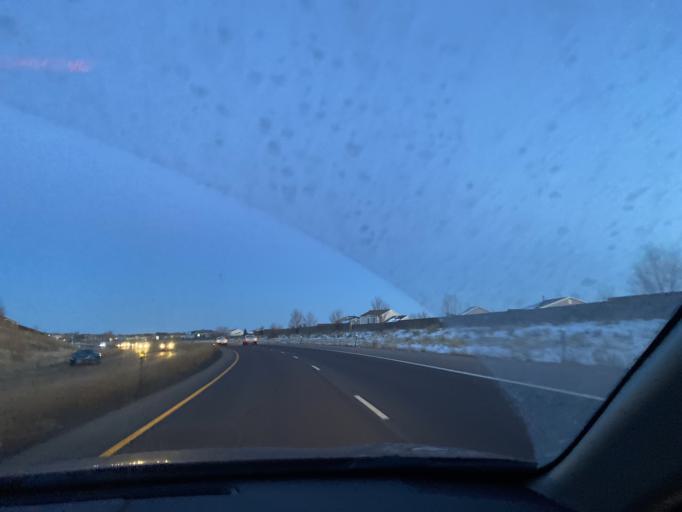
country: US
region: Colorado
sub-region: El Paso County
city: Fountain
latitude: 38.7163
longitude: -104.6925
